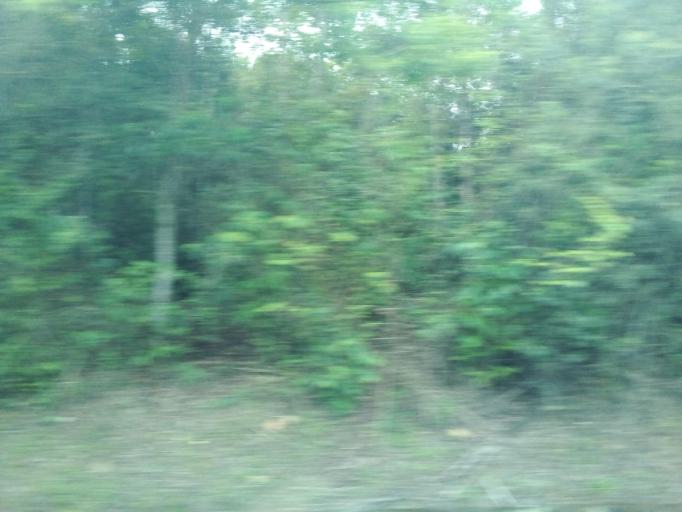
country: BR
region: Minas Gerais
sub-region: Rio Piracicaba
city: Rio Piracicaba
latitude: -19.9721
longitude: -43.2341
